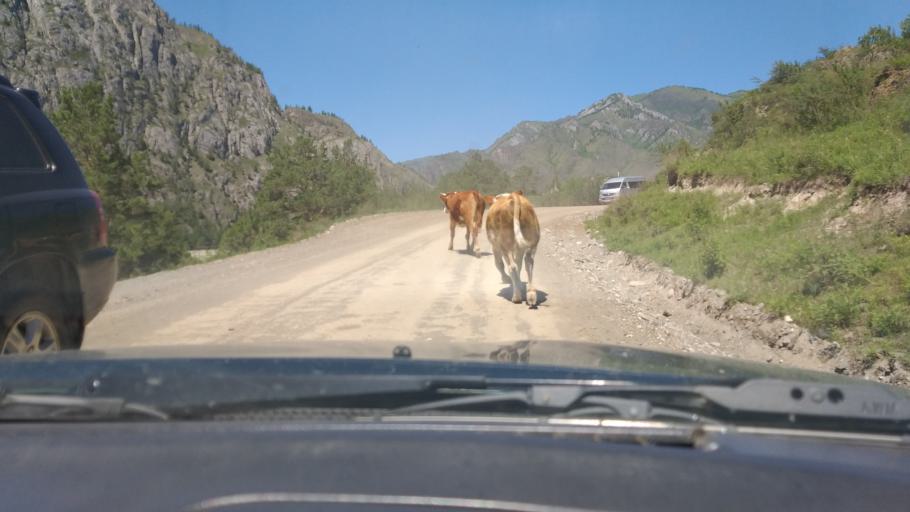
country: RU
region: Altay
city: Chemal
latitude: 51.2065
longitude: 86.0856
